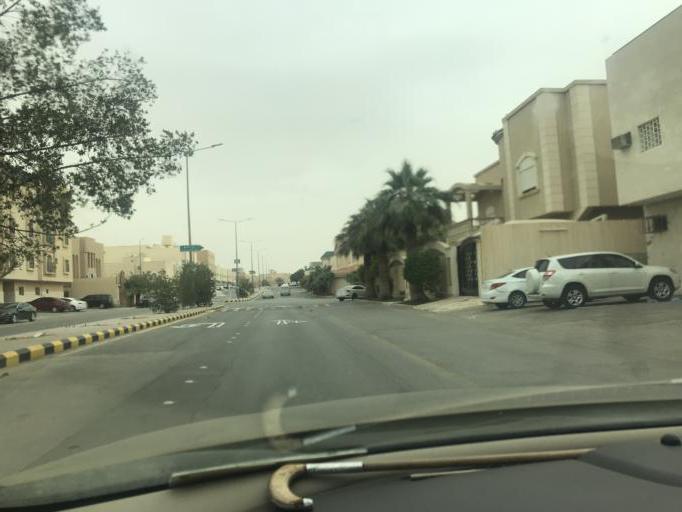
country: SA
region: Ar Riyad
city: Riyadh
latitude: 24.7384
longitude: 46.7556
